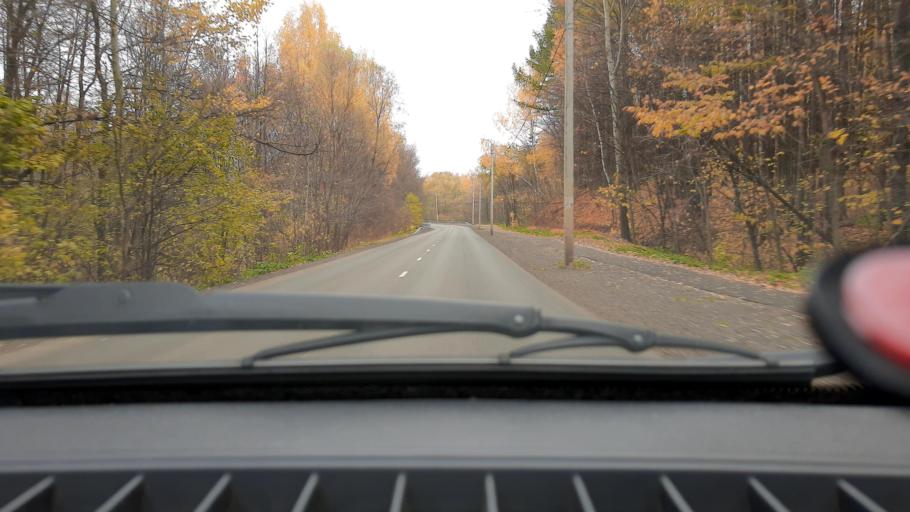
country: RU
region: Bashkortostan
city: Avdon
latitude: 54.6634
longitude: 55.7078
